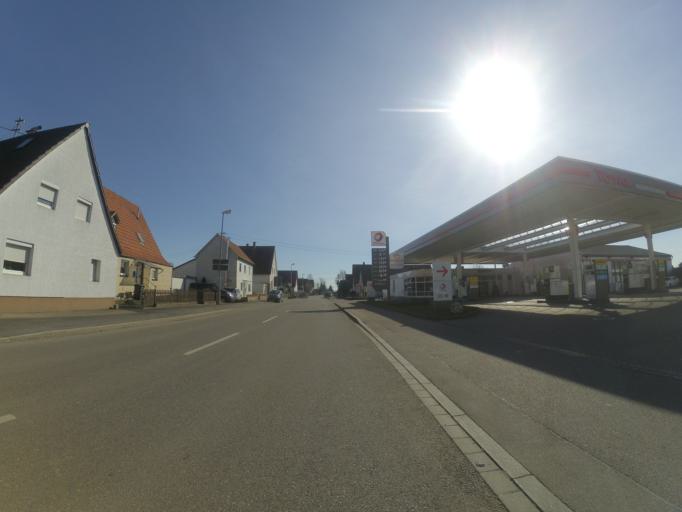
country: DE
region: Baden-Wuerttemberg
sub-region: Regierungsbezirk Stuttgart
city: Niederstotzingen
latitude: 48.5364
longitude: 10.2370
